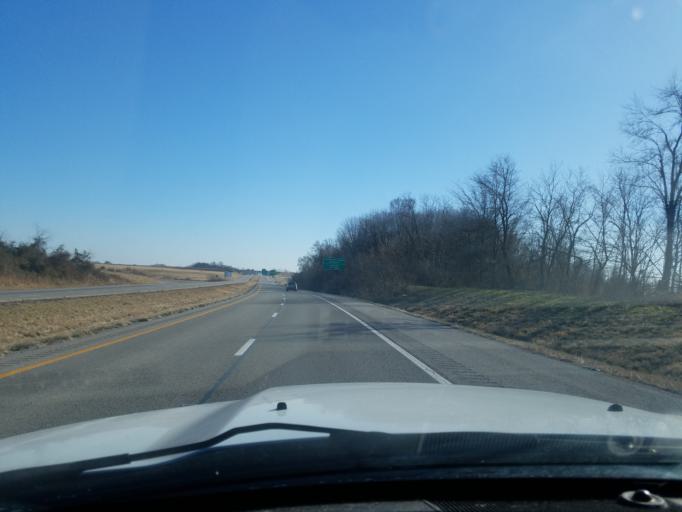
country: US
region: Kentucky
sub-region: Henderson County
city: Henderson
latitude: 37.8036
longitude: -87.5633
